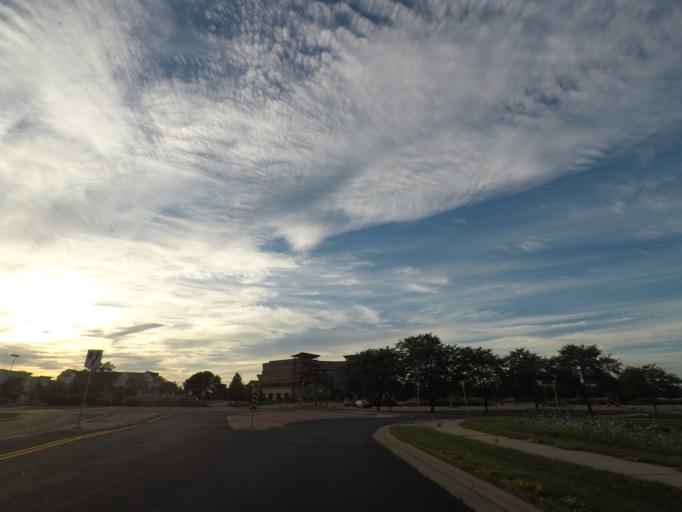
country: US
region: Wisconsin
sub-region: Dane County
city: Middleton
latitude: 43.0935
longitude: -89.5251
